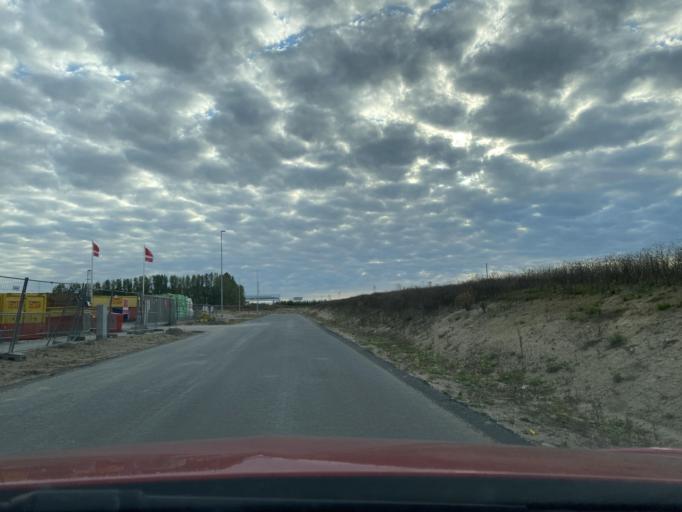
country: SE
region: Skane
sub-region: Lunds Kommun
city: Lund
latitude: 55.7317
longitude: 13.2435
